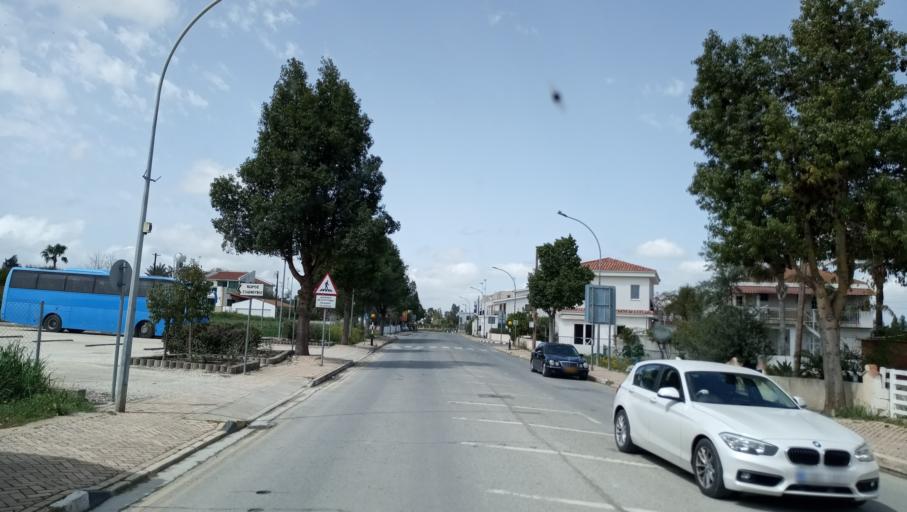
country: CY
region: Lefkosia
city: Dali
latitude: 35.0196
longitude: 33.4225
